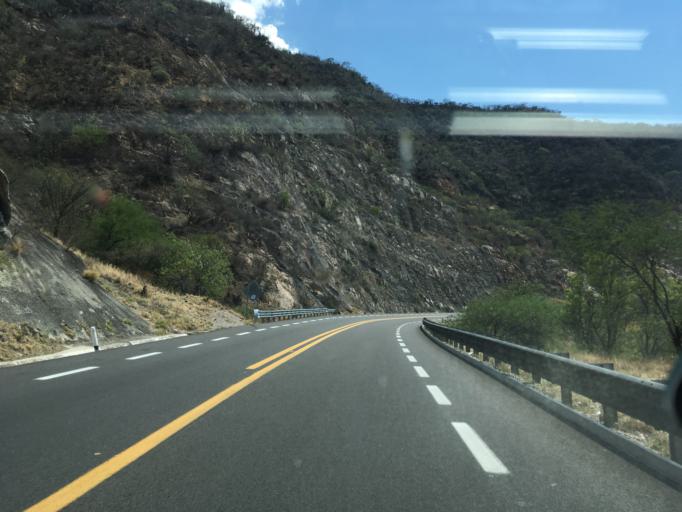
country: MX
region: Puebla
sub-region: San Jose Miahuatlan
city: San Pedro Tetitlan
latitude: 18.1534
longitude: -97.2981
